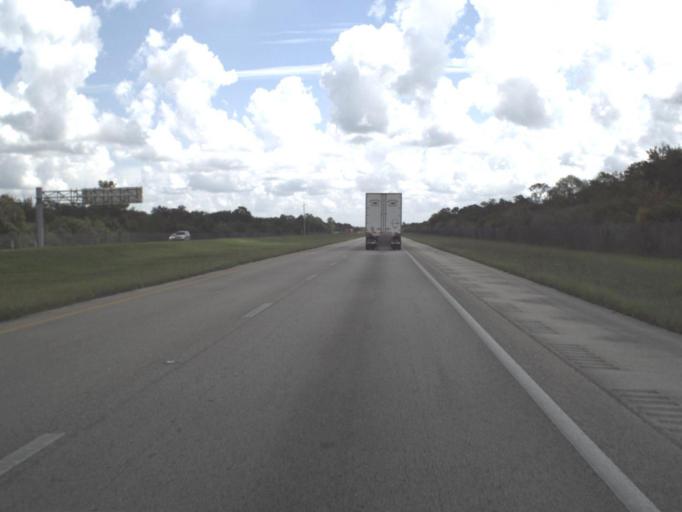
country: US
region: Florida
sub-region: Collier County
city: Orangetree
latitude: 26.1530
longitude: -81.5053
